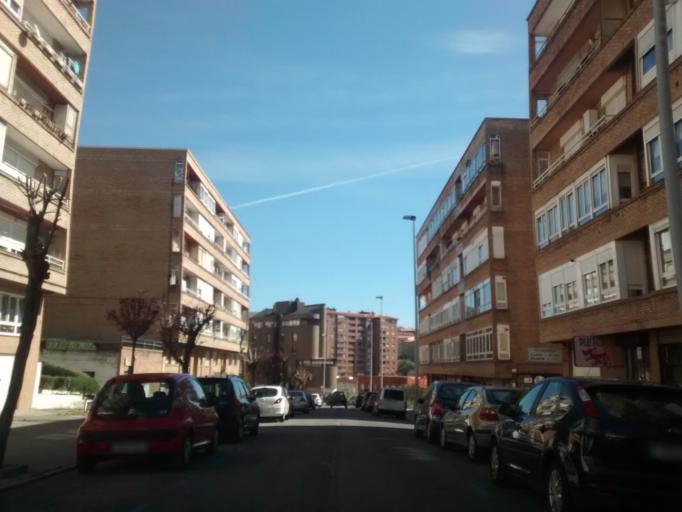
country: ES
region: Cantabria
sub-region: Provincia de Cantabria
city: Santander
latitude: 43.4652
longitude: -3.8146
